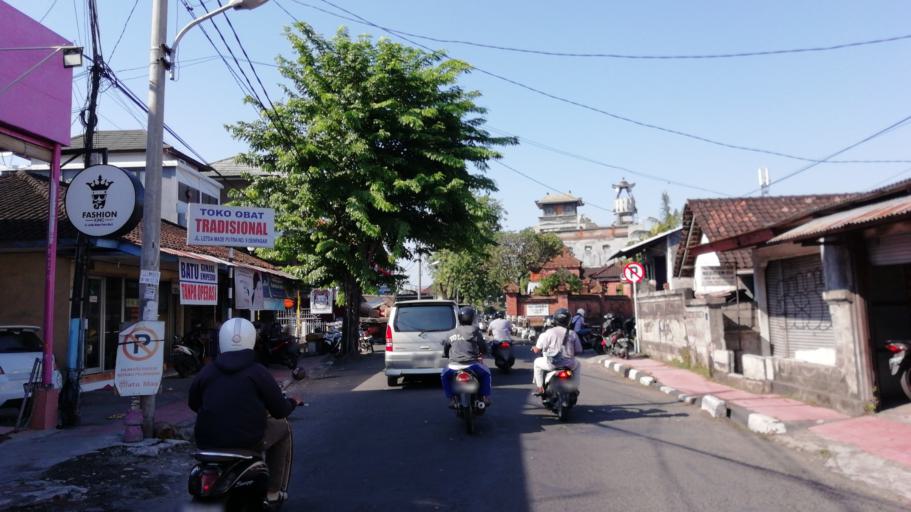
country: ID
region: Bali
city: Denpasar
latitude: -8.6588
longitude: 115.2198
